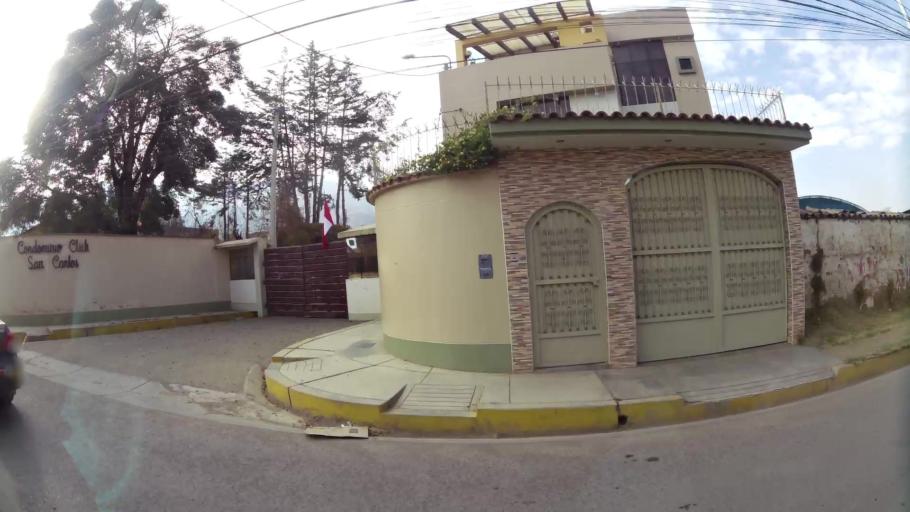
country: PE
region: Junin
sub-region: Provincia de Huancayo
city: Huancayo
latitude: -12.0436
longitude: -75.1967
